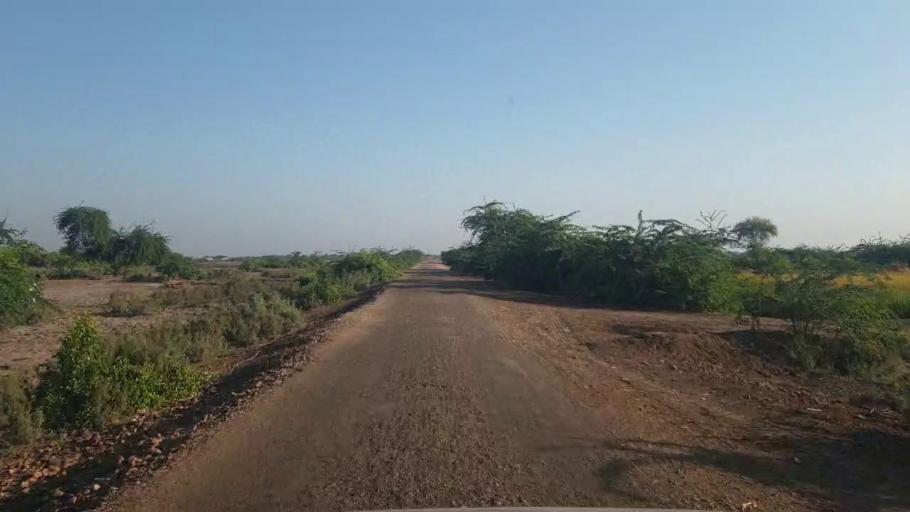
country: PK
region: Sindh
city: Badin
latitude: 24.7245
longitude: 68.8639
